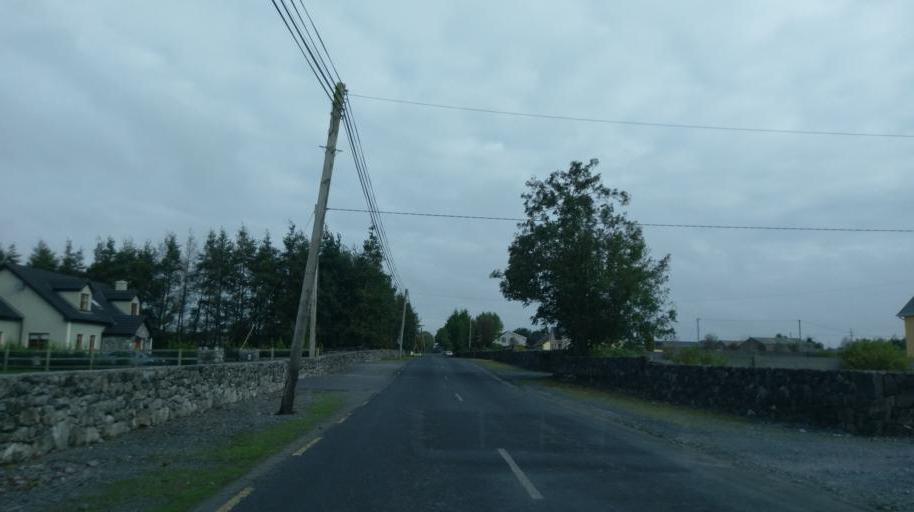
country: IE
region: Connaught
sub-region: County Galway
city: Athenry
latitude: 53.3432
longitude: -8.7133
